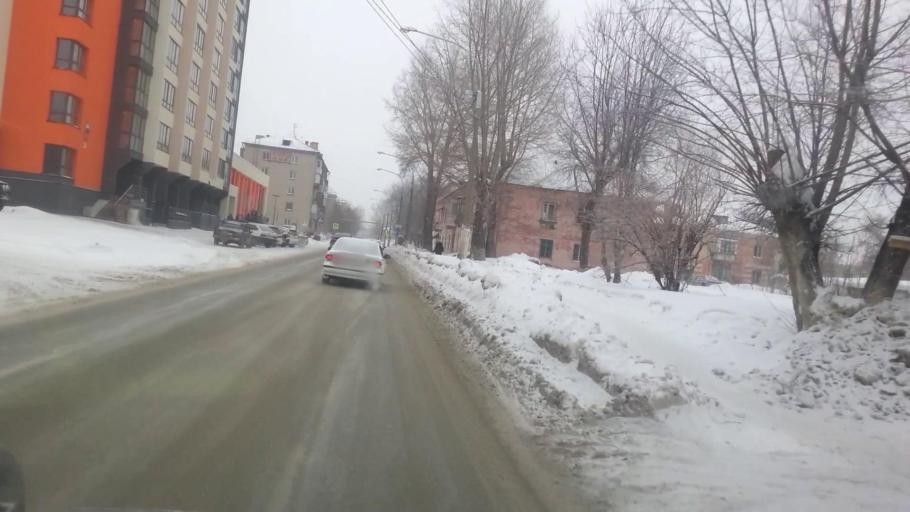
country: RU
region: Altai Krai
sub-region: Gorod Barnaulskiy
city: Barnaul
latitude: 53.3795
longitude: 83.7300
